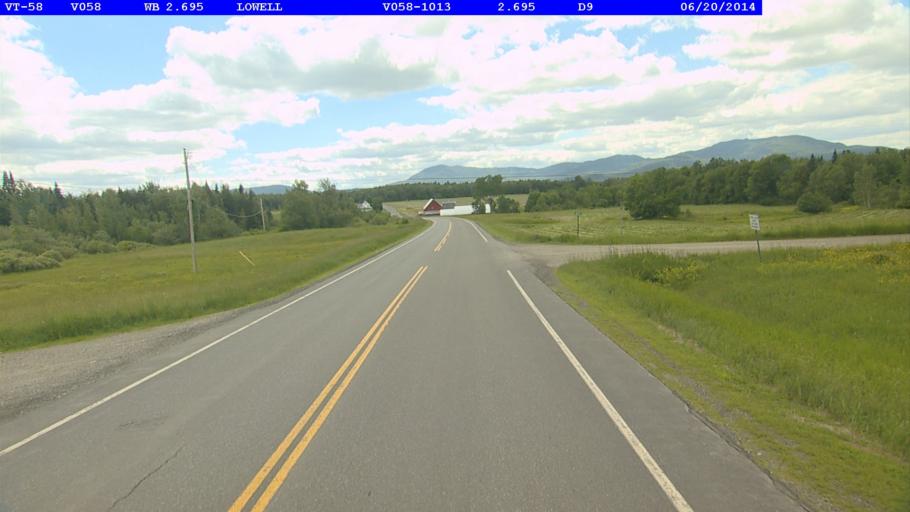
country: US
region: Vermont
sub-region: Orleans County
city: Newport
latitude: 44.8112
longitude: -72.4027
